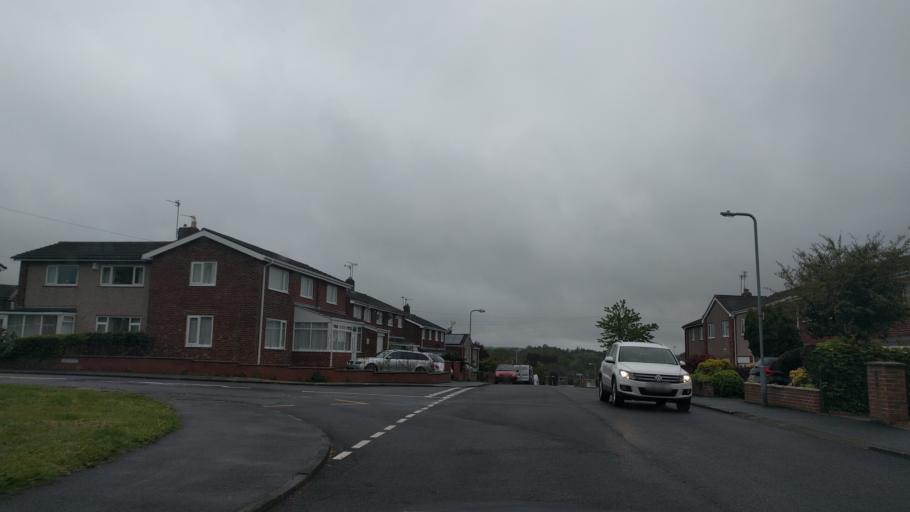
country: GB
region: England
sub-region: Northumberland
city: Morpeth
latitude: 55.1605
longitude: -1.7014
